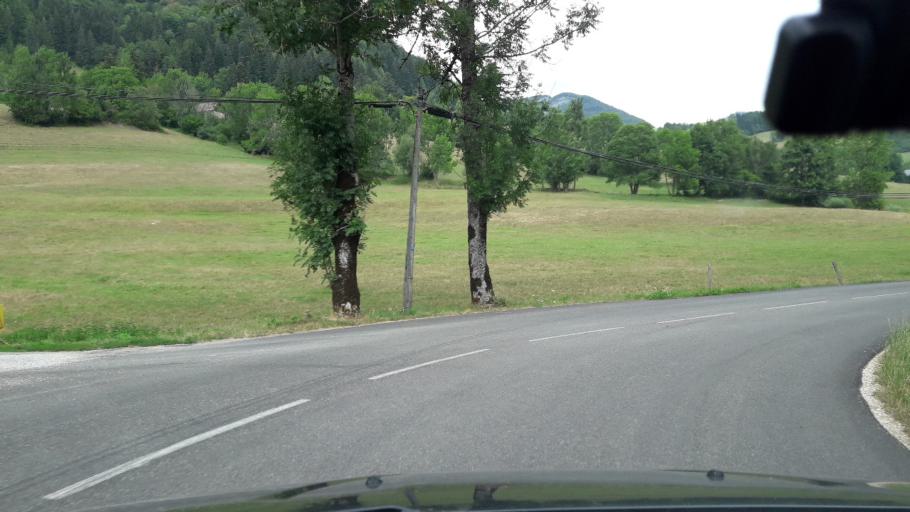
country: FR
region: Rhone-Alpes
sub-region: Departement de la Savoie
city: Vimines
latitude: 45.4519
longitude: 5.8778
